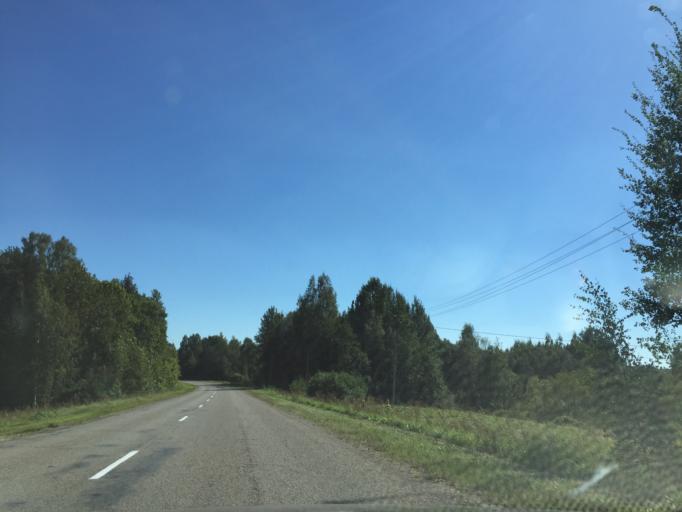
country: LV
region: Akniste
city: Akniste
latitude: 56.0572
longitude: 25.9002
